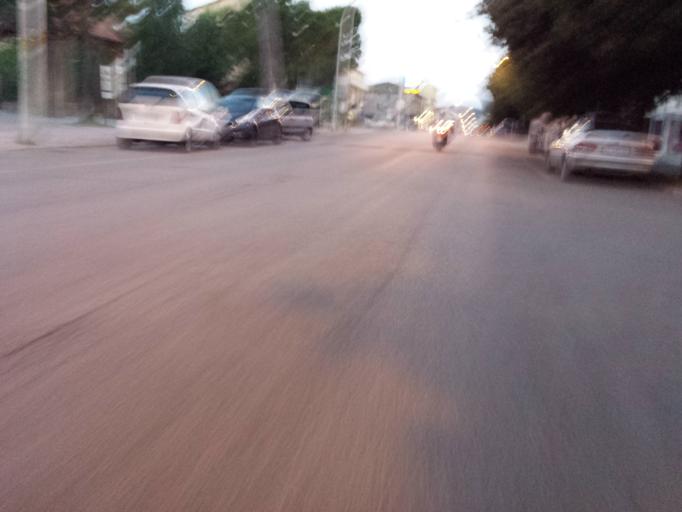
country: IT
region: Molise
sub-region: Provincia di Campobasso
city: Campobasso
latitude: 41.5674
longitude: 14.6729
